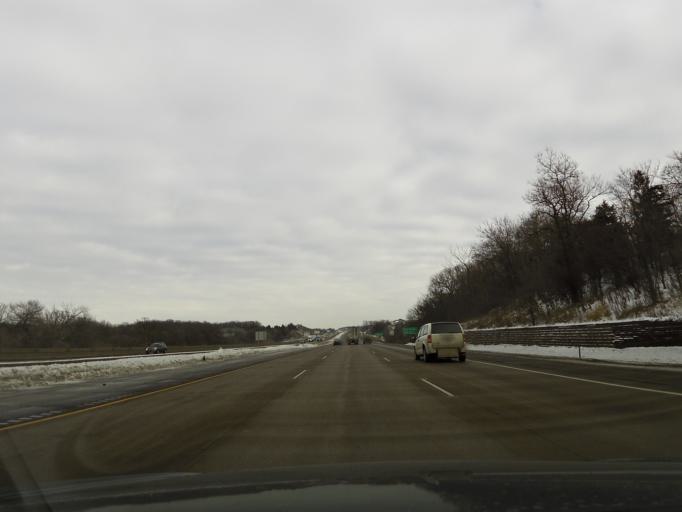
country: US
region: Wisconsin
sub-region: Saint Croix County
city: Hudson
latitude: 44.9638
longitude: -92.7122
